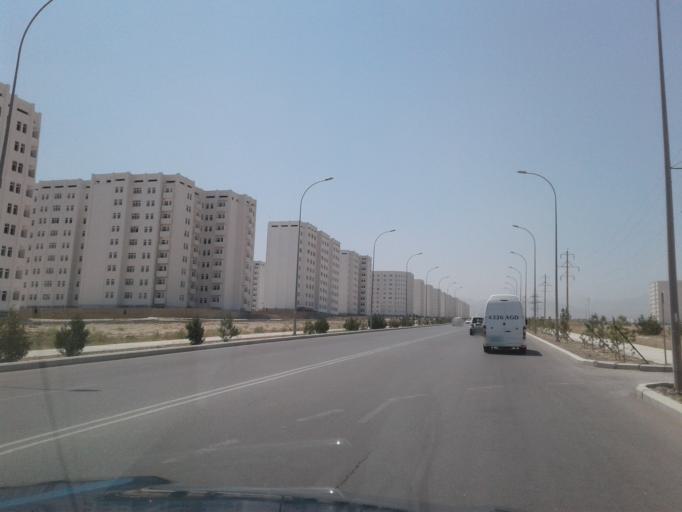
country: TM
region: Ahal
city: Ashgabat
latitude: 37.8989
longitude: 58.4056
